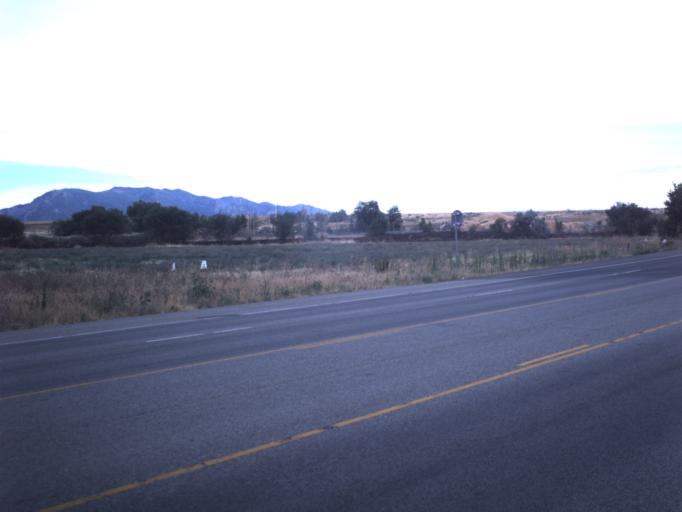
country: US
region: Utah
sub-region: Weber County
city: West Haven
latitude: 41.2039
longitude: -112.0259
